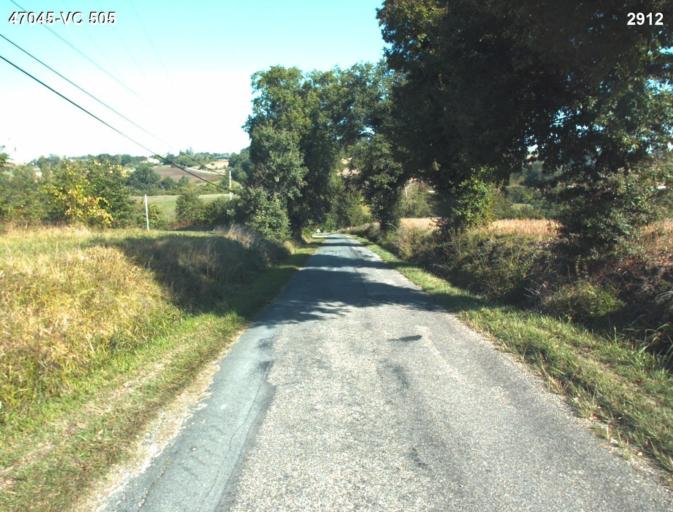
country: FR
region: Aquitaine
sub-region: Departement du Lot-et-Garonne
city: Nerac
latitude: 44.1389
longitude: 0.4161
